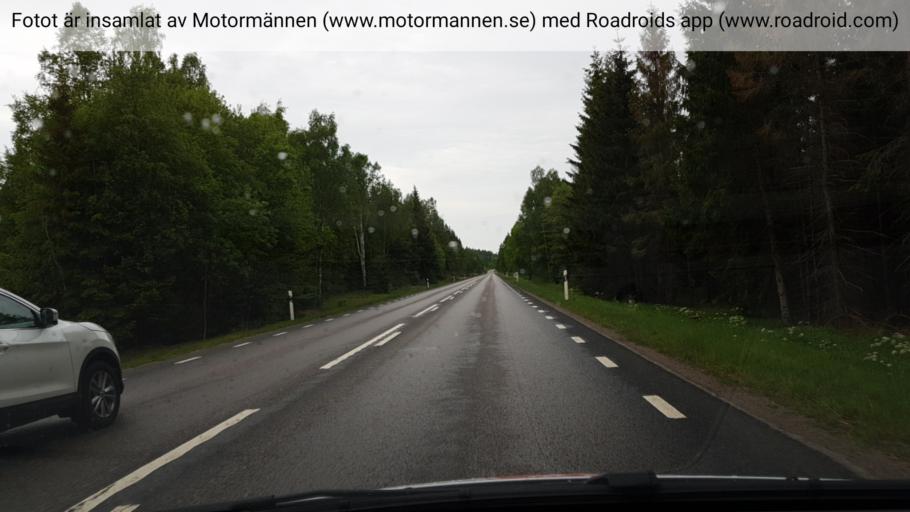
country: SE
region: Kalmar
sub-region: Hultsfreds Kommun
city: Hultsfred
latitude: 57.5428
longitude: 15.8461
